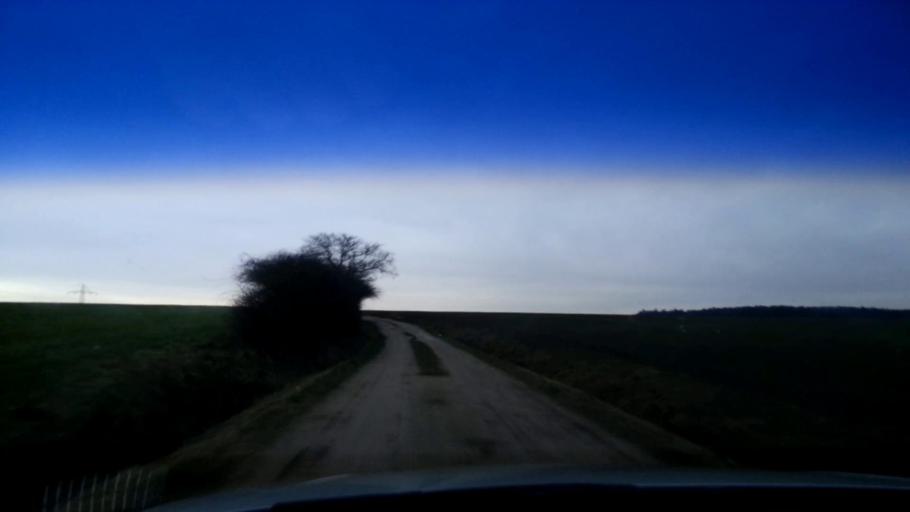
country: DE
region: Bavaria
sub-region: Upper Franconia
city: Litzendorf
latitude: 49.9184
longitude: 10.9887
